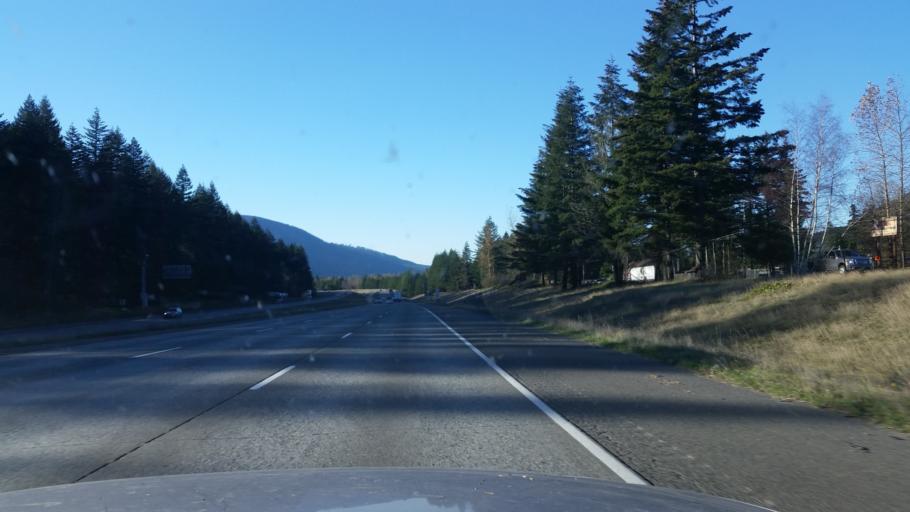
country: US
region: Washington
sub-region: King County
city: Tanner
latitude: 47.4705
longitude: -121.7314
